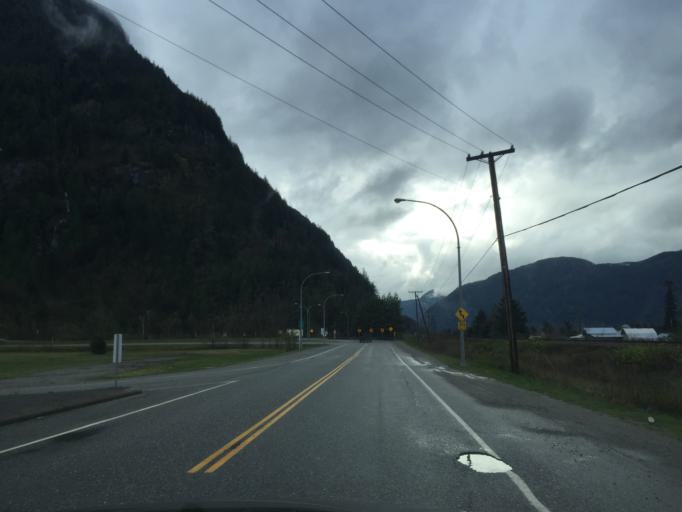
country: CA
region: British Columbia
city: Hope
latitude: 49.3654
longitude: -121.5196
